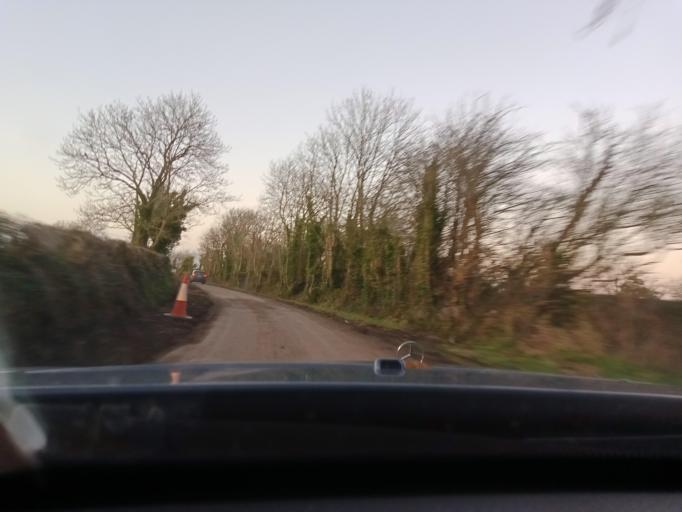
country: IE
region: Leinster
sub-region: Kilkenny
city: Callan
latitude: 52.4478
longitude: -7.3950
